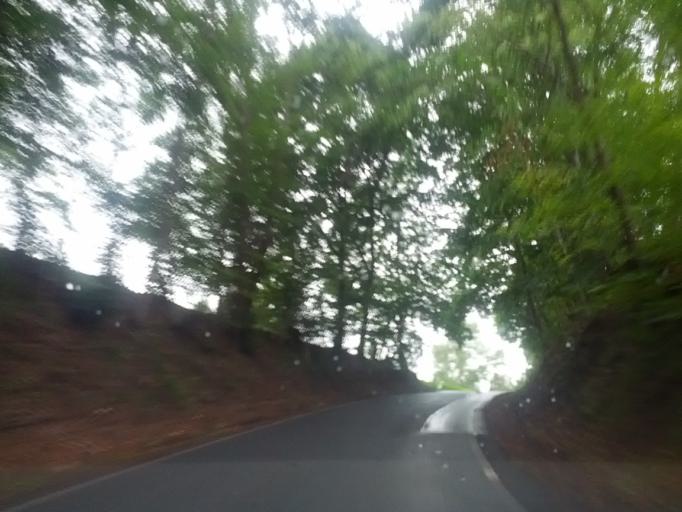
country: DE
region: Thuringia
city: Tabarz
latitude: 50.9085
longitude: 10.4834
